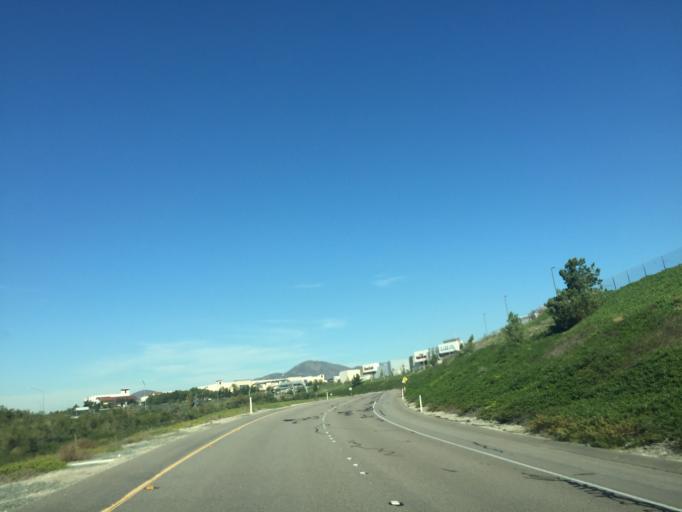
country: US
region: California
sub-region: San Diego County
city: Bonita
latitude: 32.6177
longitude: -116.9709
